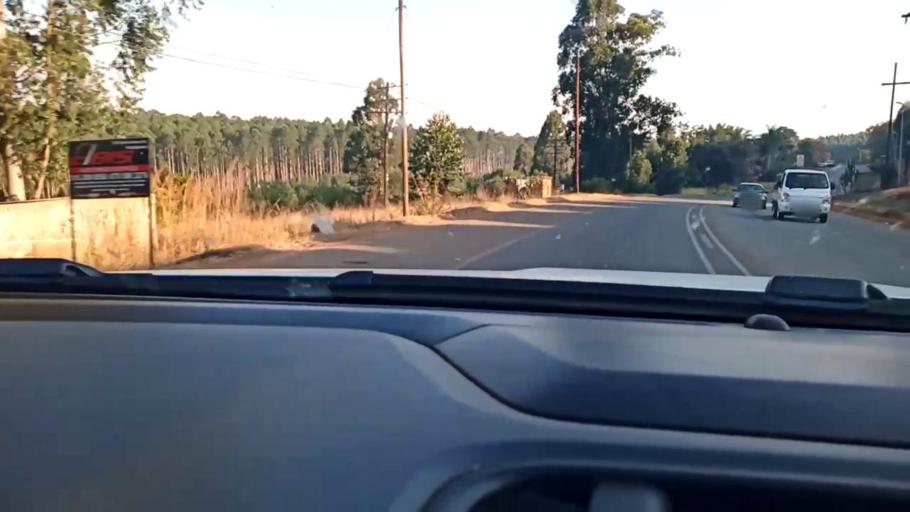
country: ZA
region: Limpopo
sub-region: Mopani District Municipality
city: Duiwelskloof
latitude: -23.7006
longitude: 30.1356
